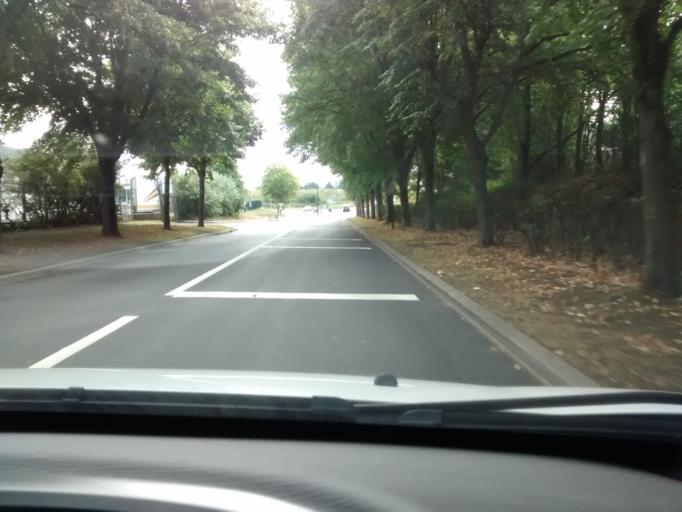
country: FR
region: Ile-de-France
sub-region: Departement des Yvelines
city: Buc
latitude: 48.7658
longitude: 2.1255
